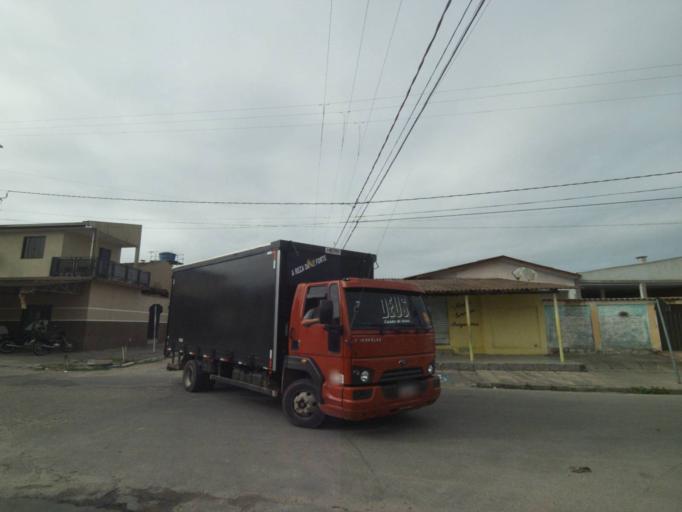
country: BR
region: Parana
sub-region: Paranagua
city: Paranagua
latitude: -25.5144
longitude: -48.5319
